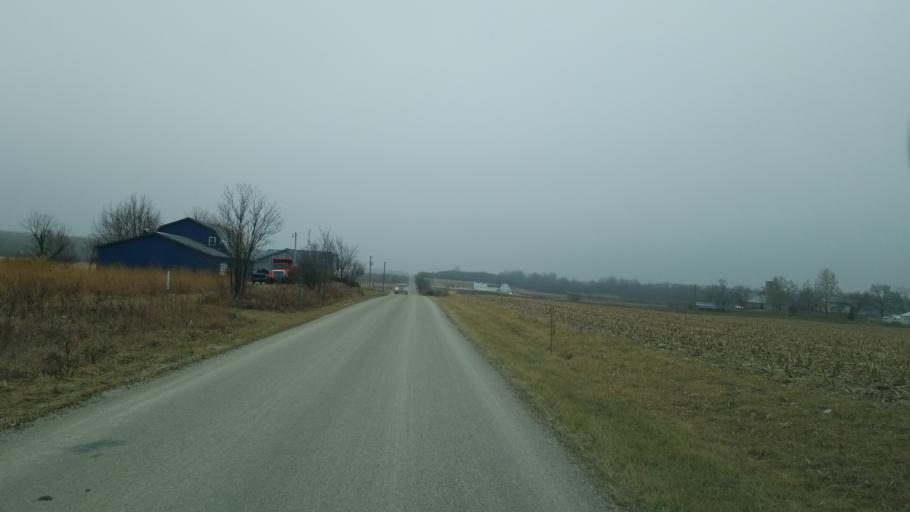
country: US
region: Indiana
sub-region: Adams County
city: Geneva
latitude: 40.5498
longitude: -85.0300
